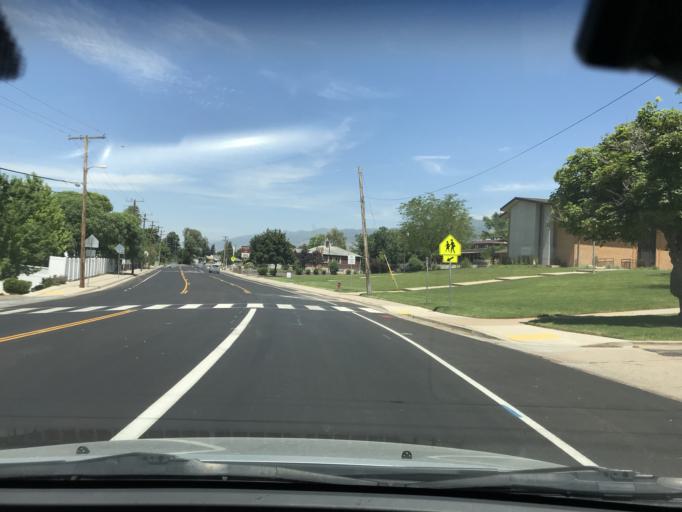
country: US
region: Utah
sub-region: Davis County
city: North Salt Lake
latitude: 40.8502
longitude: -111.8962
